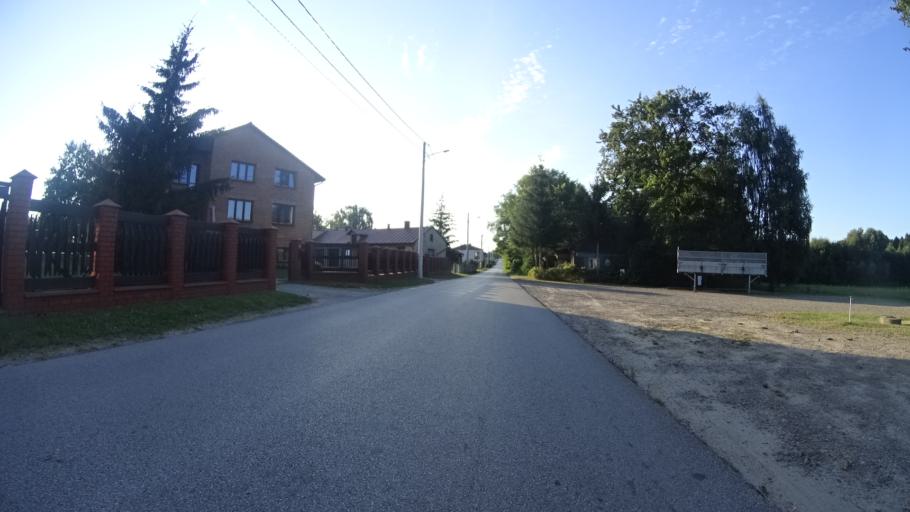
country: PL
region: Masovian Voivodeship
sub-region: Powiat grojecki
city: Goszczyn
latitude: 51.6970
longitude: 20.8110
